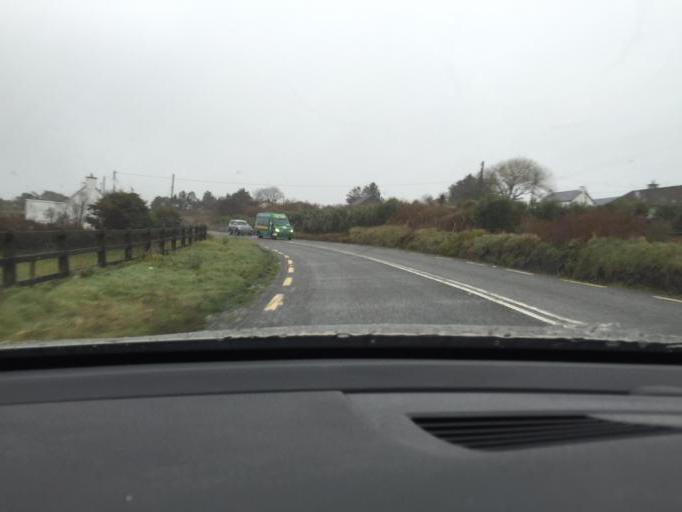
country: IE
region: Munster
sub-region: Ciarrai
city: Dingle
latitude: 52.1442
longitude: -10.1396
